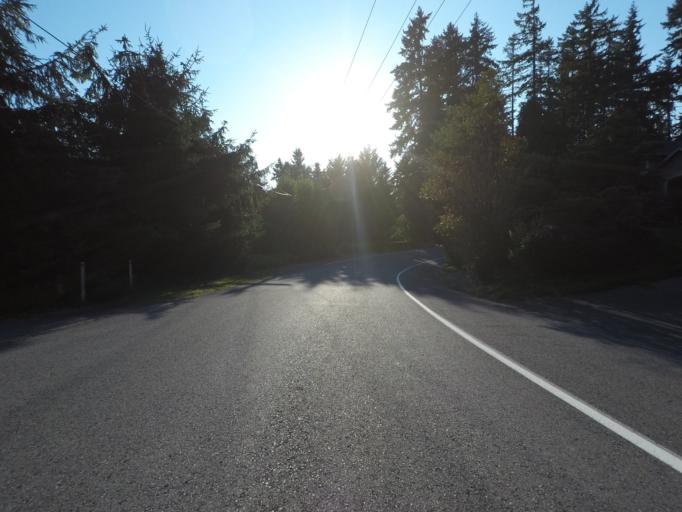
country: US
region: Washington
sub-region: King County
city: Kenmore
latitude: 47.7479
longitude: -122.2387
